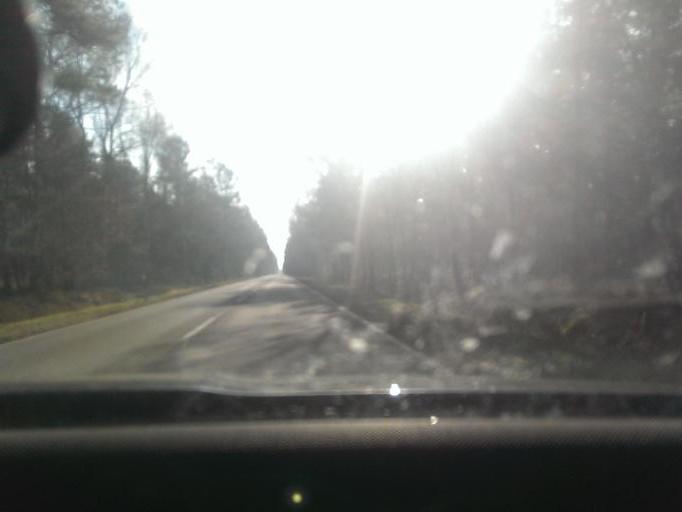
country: DE
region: Lower Saxony
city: Lindwedel
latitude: 52.6350
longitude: 9.6903
